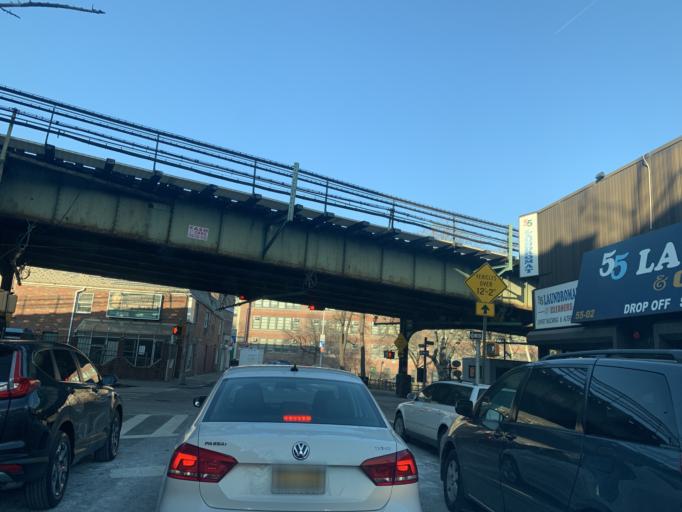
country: US
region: New York
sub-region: Queens County
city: Long Island City
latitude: 40.7448
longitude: -73.9096
